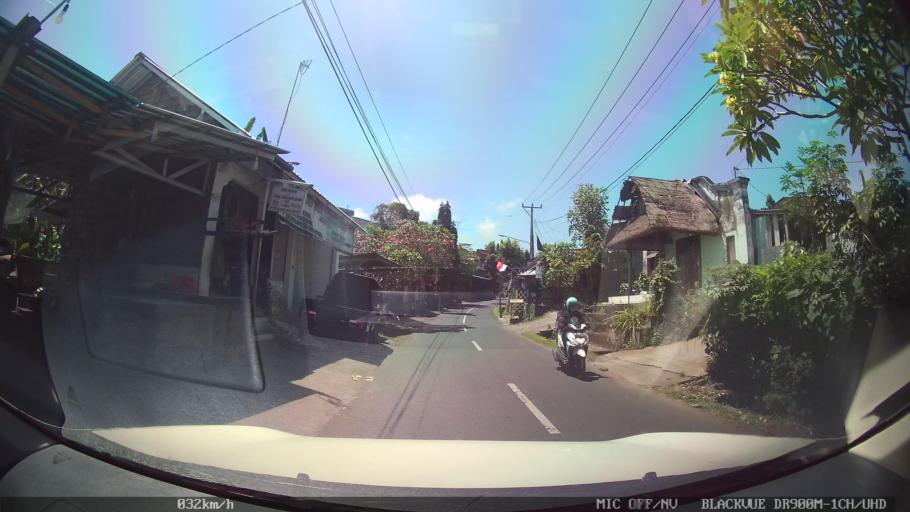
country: ID
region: Bali
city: Banjar Pasekan
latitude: -8.5780
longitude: 115.3213
